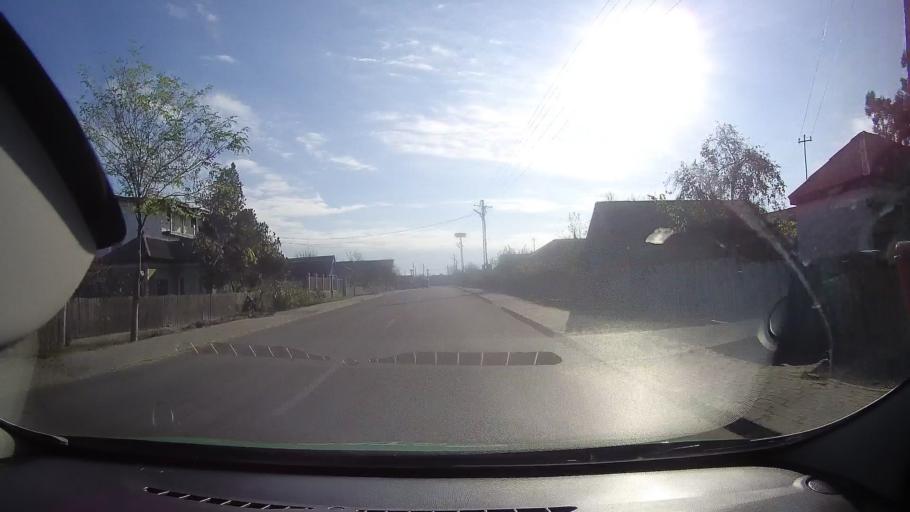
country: RO
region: Tulcea
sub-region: Comuna Murighiol
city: Murighiol
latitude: 45.0392
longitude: 29.1588
